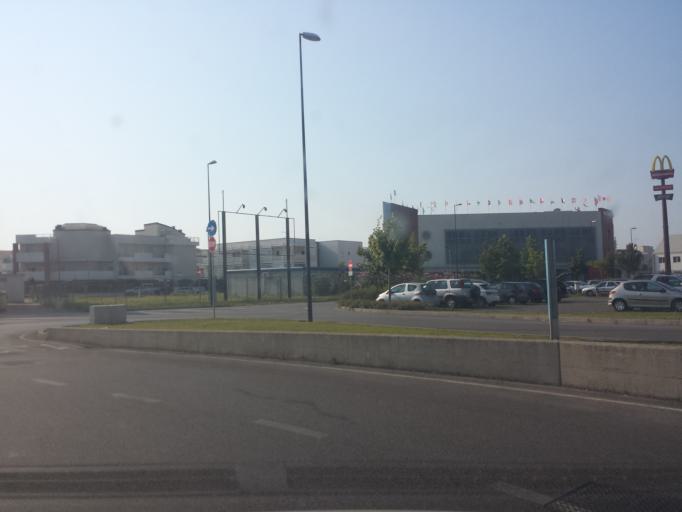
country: IT
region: Veneto
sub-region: Provincia di Venezia
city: Lido di Iesolo
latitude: 45.5067
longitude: 12.6345
